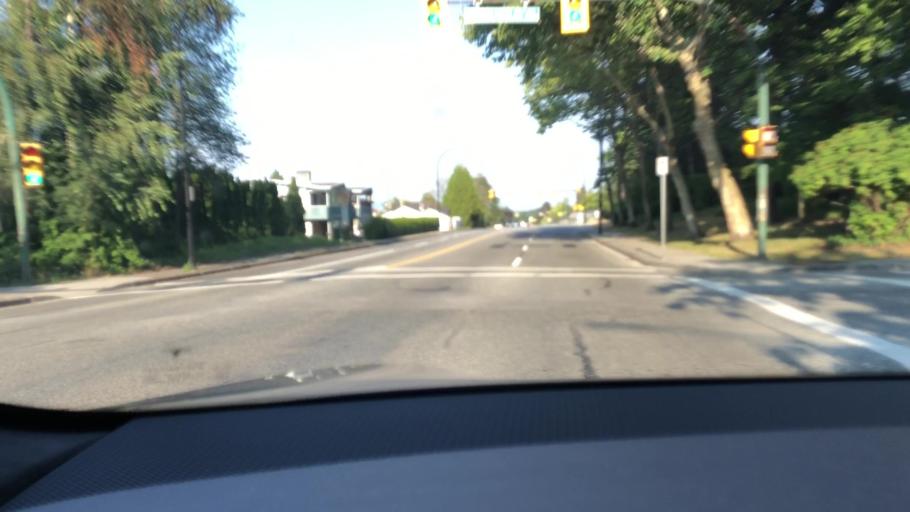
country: CA
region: British Columbia
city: Burnaby
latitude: 49.2299
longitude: -122.9966
